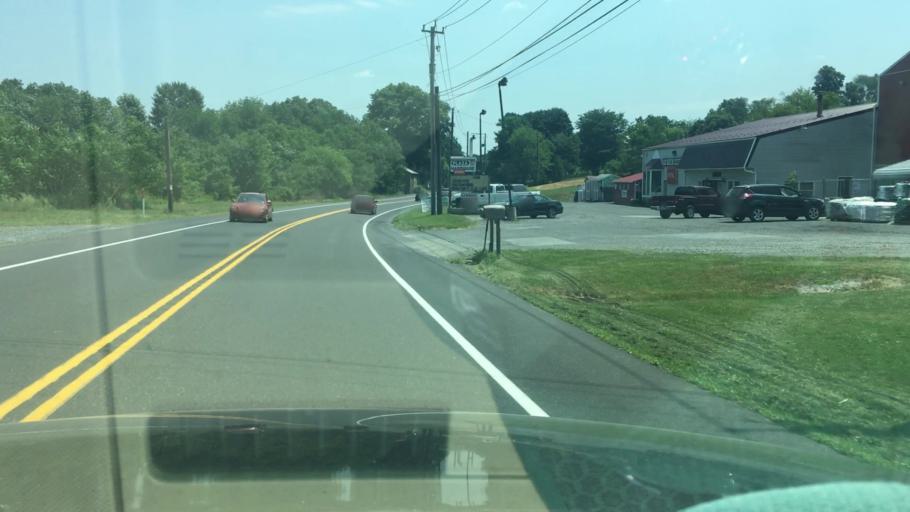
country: US
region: Pennsylvania
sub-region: Lehigh County
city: Schnecksville
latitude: 40.6801
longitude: -75.7066
